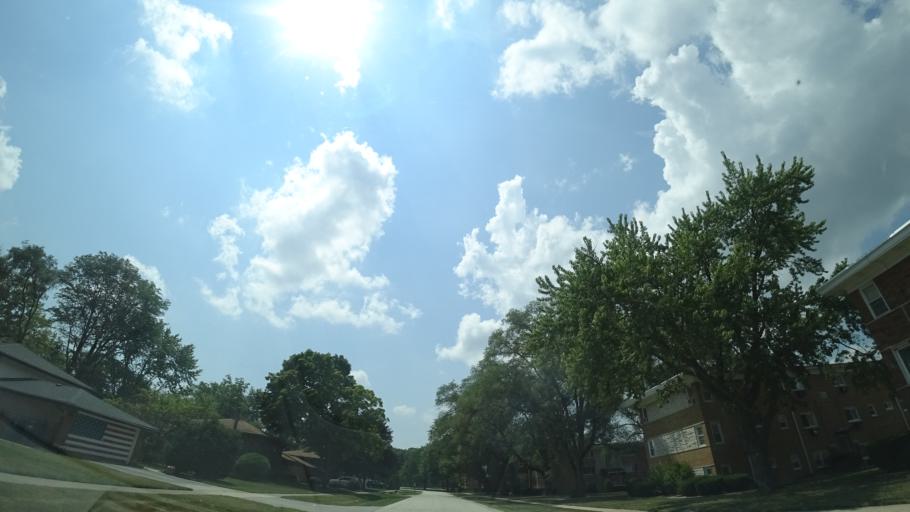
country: US
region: Illinois
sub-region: Cook County
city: Worth
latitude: 41.6949
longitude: -87.7901
